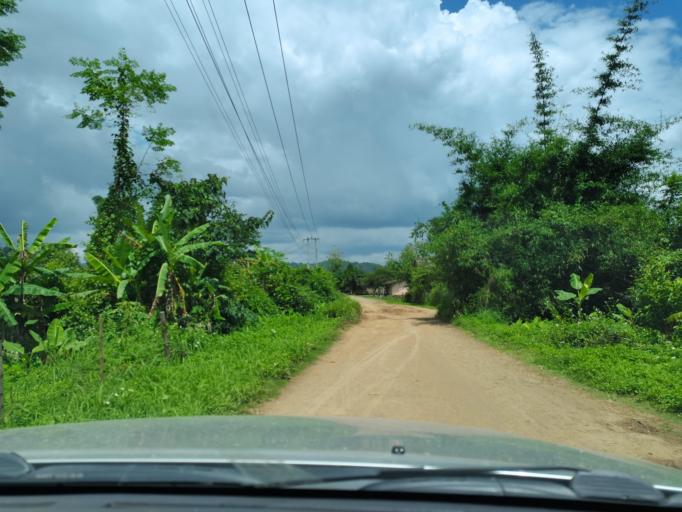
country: LA
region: Loungnamtha
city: Muang Long
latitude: 20.6817
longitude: 101.0522
